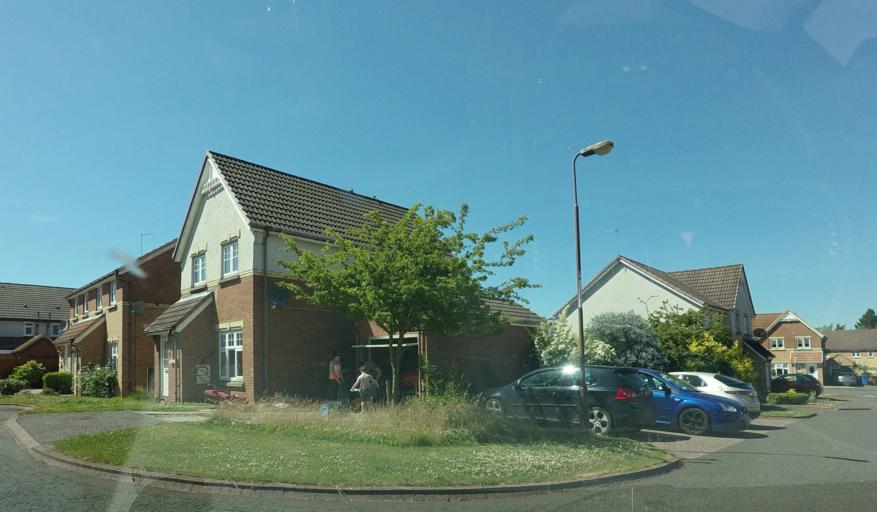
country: GB
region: Scotland
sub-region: West Lothian
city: Broxburn
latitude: 55.9314
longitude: -3.4786
